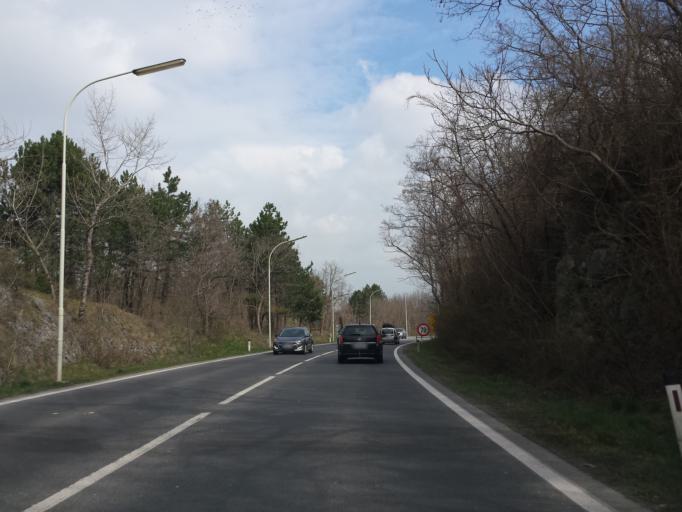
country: AT
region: Lower Austria
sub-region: Politischer Bezirk Bruck an der Leitha
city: Bad Deutsch-Altenburg
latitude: 48.1378
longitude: 16.9109
